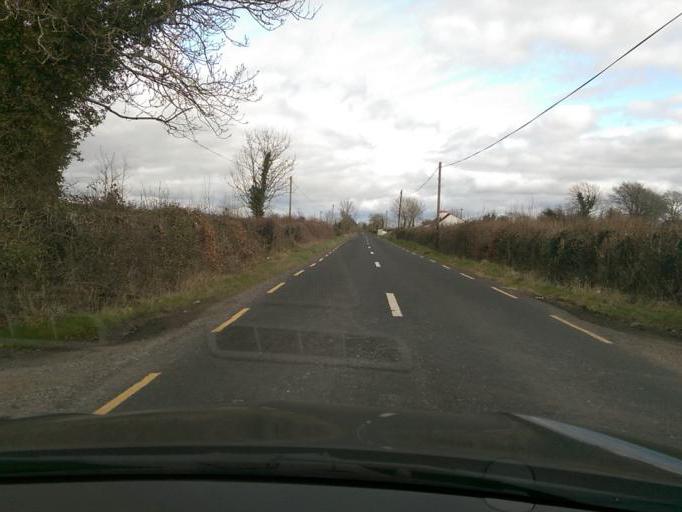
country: IE
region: Connaught
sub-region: County Galway
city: Ballinasloe
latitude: 53.3321
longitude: -8.3422
